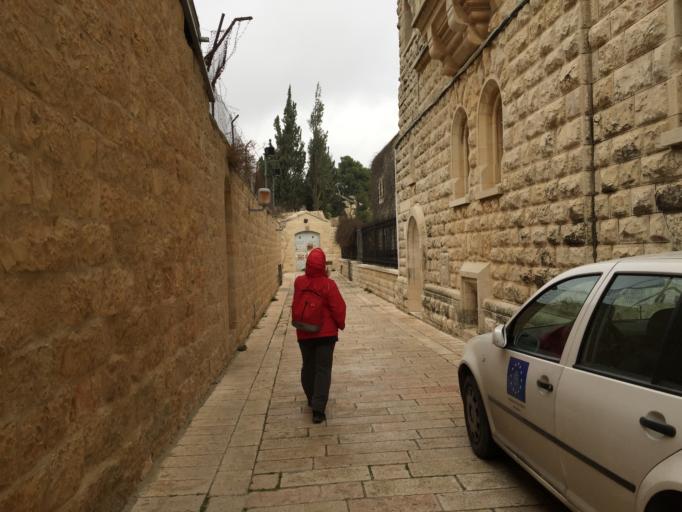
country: PS
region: West Bank
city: Old City
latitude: 31.7718
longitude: 35.2287
